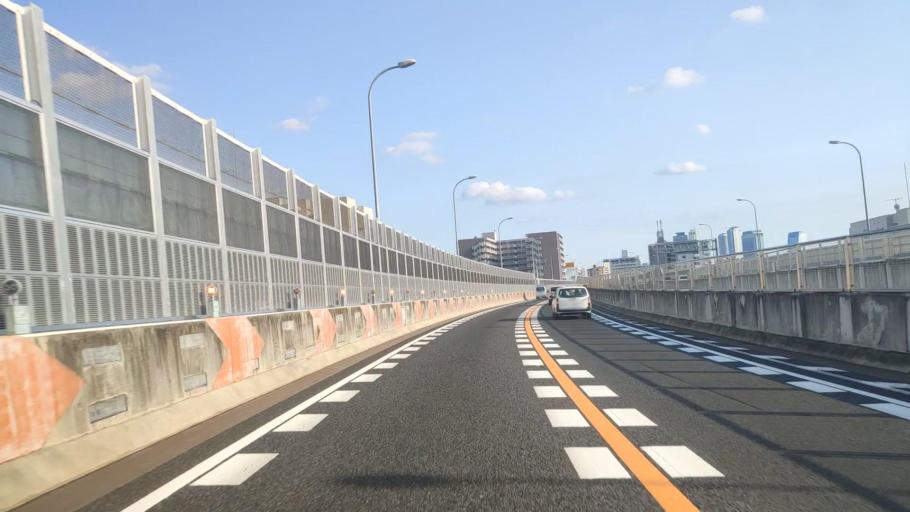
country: JP
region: Aichi
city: Nagoya-shi
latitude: 35.2011
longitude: 136.8909
